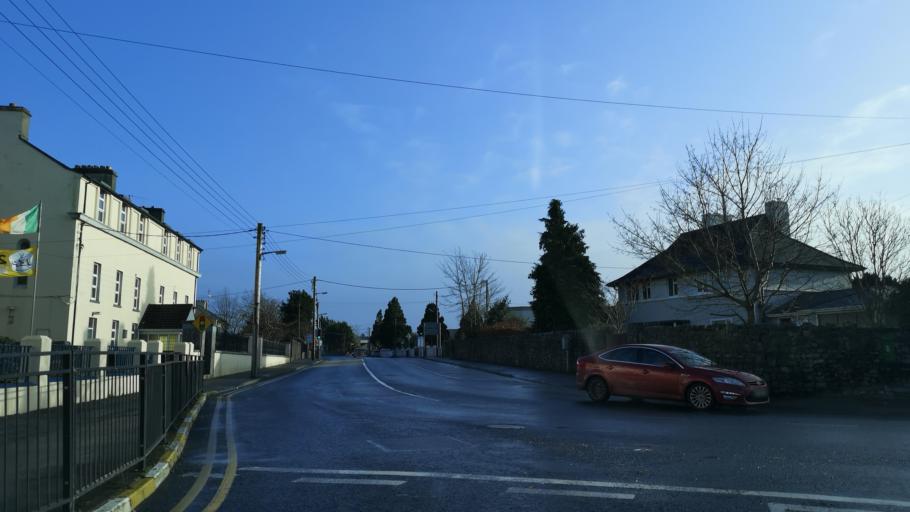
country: IE
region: Connaught
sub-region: County Galway
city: Tuam
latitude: 53.5123
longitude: -8.8475
